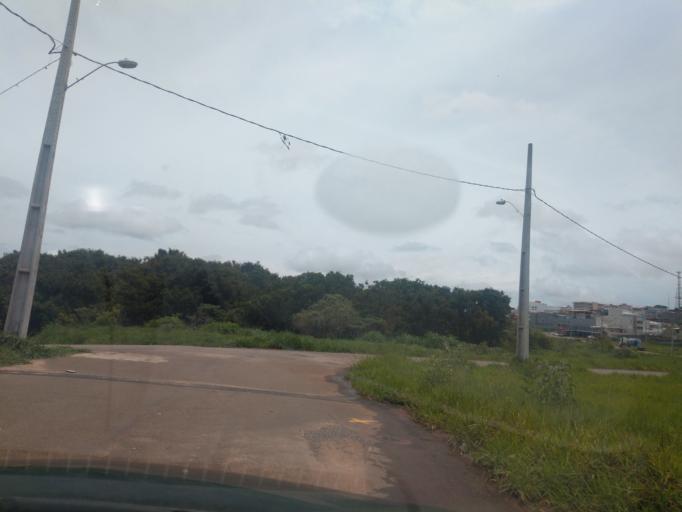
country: BR
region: Minas Gerais
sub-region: Tres Coracoes
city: Tres Coracoes
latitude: -21.6800
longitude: -45.2616
